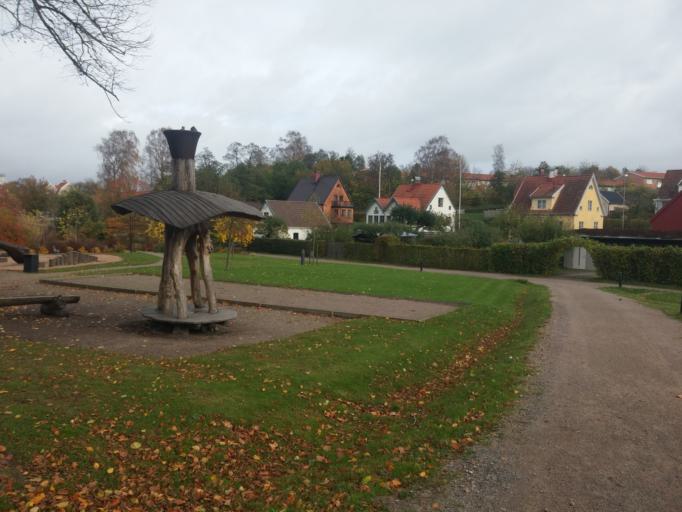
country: SE
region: Halland
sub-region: Laholms Kommun
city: Laholm
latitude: 56.5083
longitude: 13.0451
